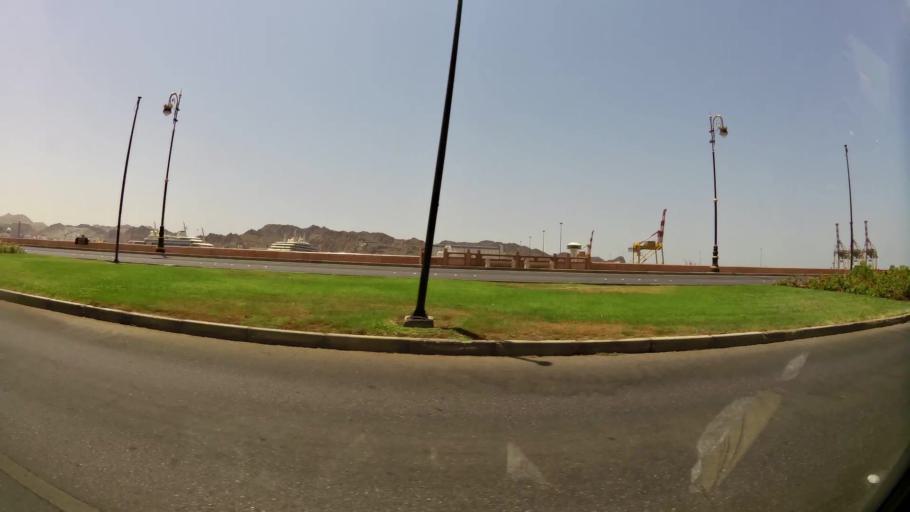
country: OM
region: Muhafazat Masqat
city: Muscat
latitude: 23.6221
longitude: 58.5698
